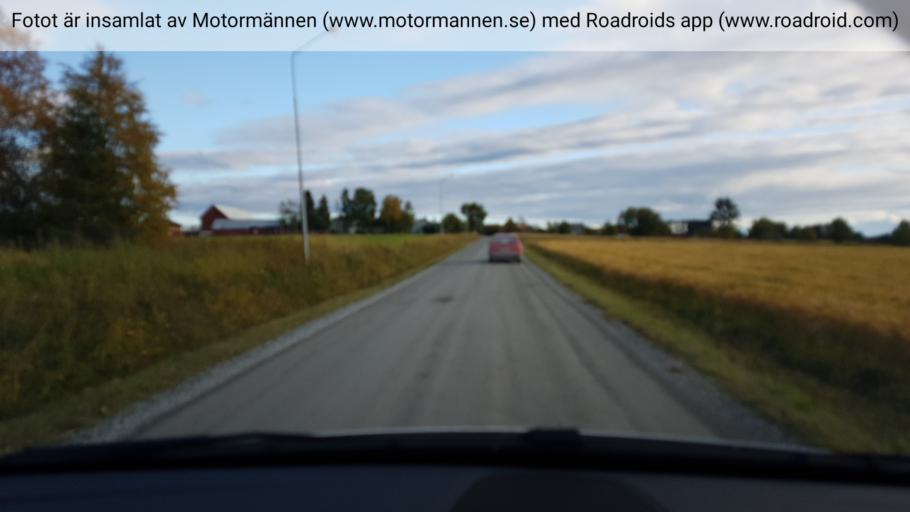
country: SE
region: Jaemtland
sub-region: Bergs Kommun
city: Hoverberg
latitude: 63.0287
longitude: 14.3715
